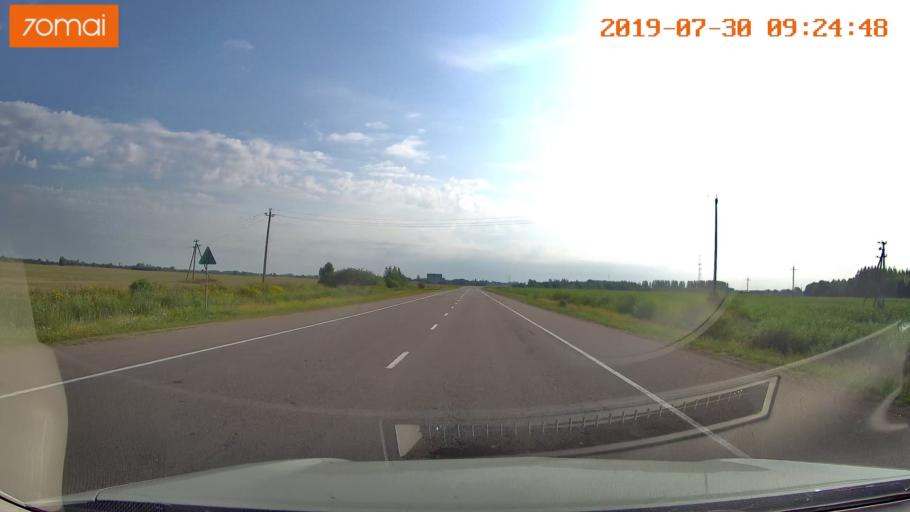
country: LT
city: Kybartai
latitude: 54.6351
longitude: 22.7026
